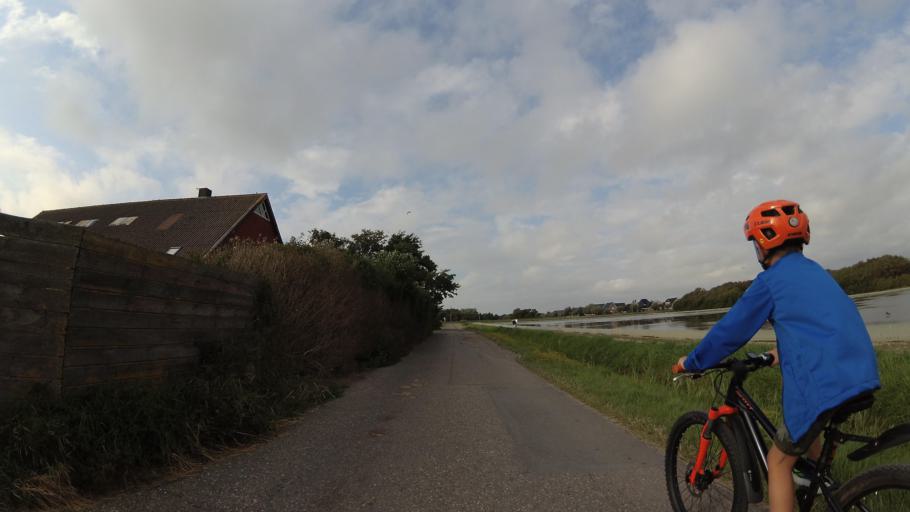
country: NL
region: North Holland
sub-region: Gemeente Den Helder
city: Den Helder
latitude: 52.8804
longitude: 4.7269
